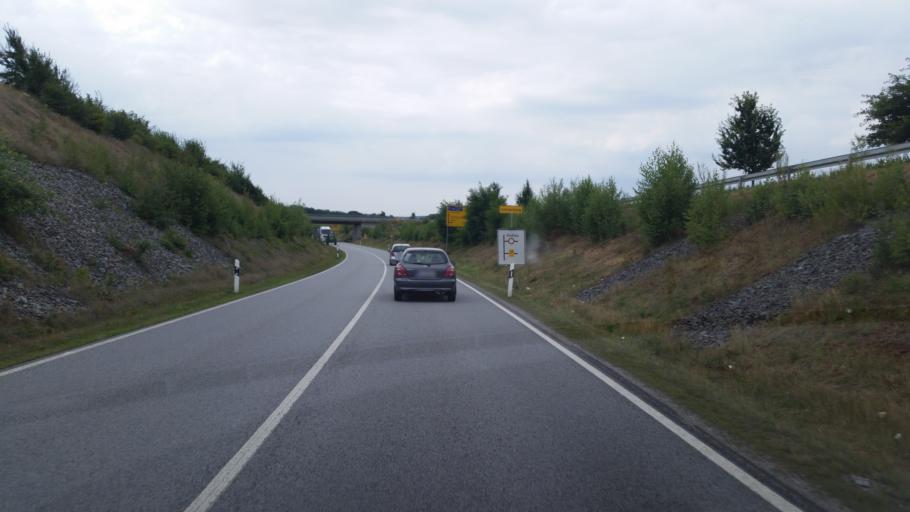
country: DE
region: Saxony
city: Elstra
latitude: 51.2276
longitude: 14.1472
